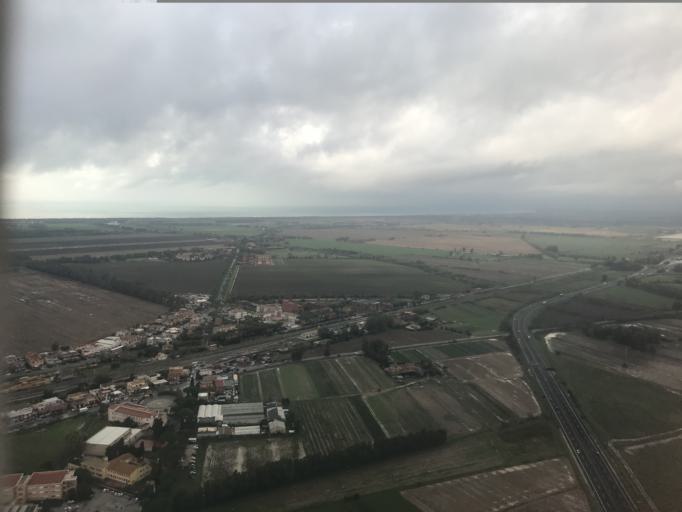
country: IT
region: Latium
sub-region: Citta metropolitana di Roma Capitale
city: Maccarese
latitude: 41.8783
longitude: 12.2484
